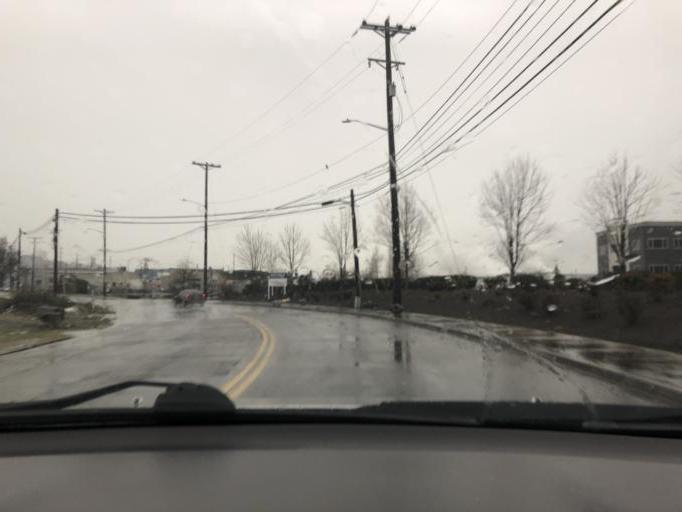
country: US
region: Washington
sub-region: Pierce County
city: Tacoma
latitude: 47.2530
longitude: -122.4239
